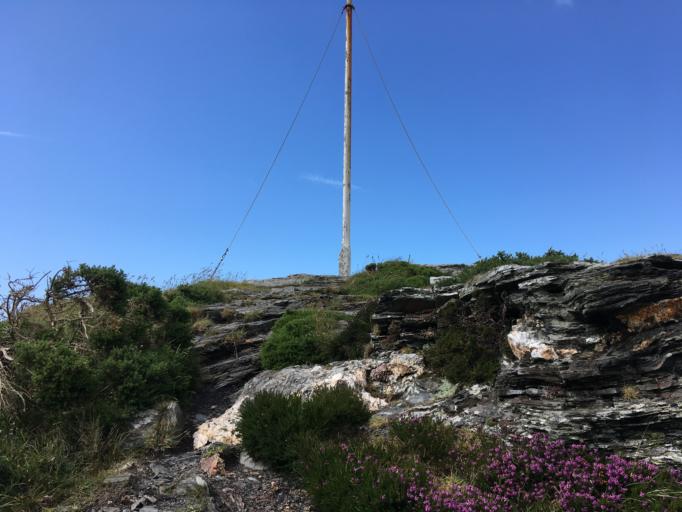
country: GB
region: England
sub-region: Cornwall
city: Tintagel
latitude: 50.6931
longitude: -4.6967
